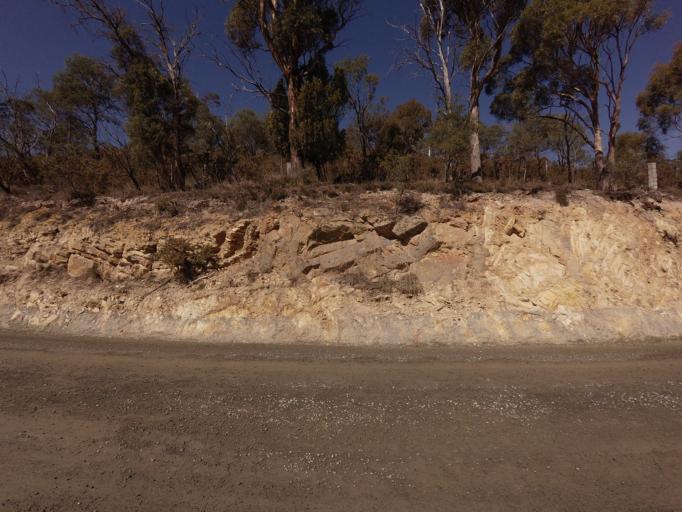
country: AU
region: Tasmania
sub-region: Break O'Day
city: St Helens
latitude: -41.6586
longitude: 147.9153
